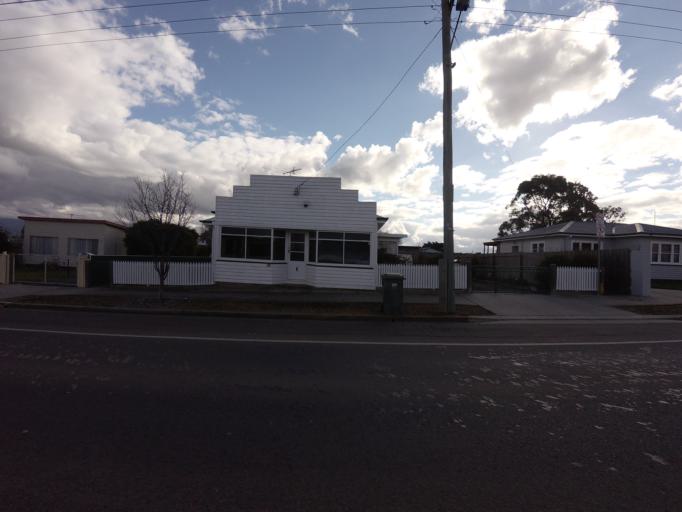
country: AU
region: Tasmania
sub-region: Northern Midlands
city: Longford
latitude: -41.6830
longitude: 147.0809
